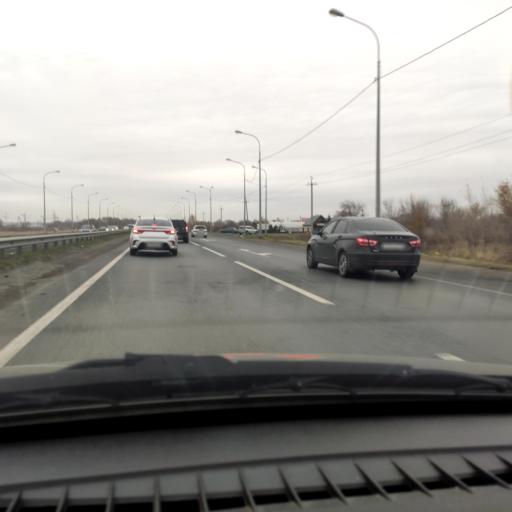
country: RU
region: Samara
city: Tol'yatti
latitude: 53.5752
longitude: 49.4406
